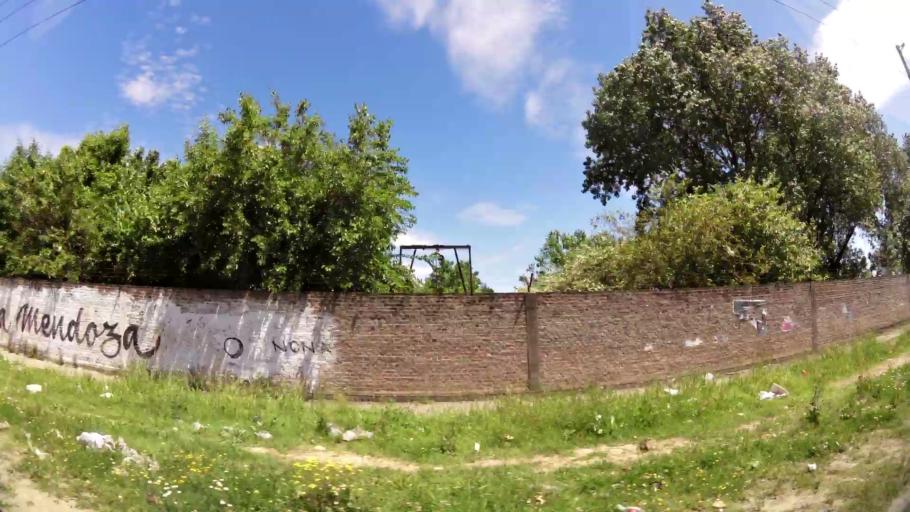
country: AR
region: Buenos Aires
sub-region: Partido de Lanus
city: Lanus
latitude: -34.7281
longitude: -58.3317
